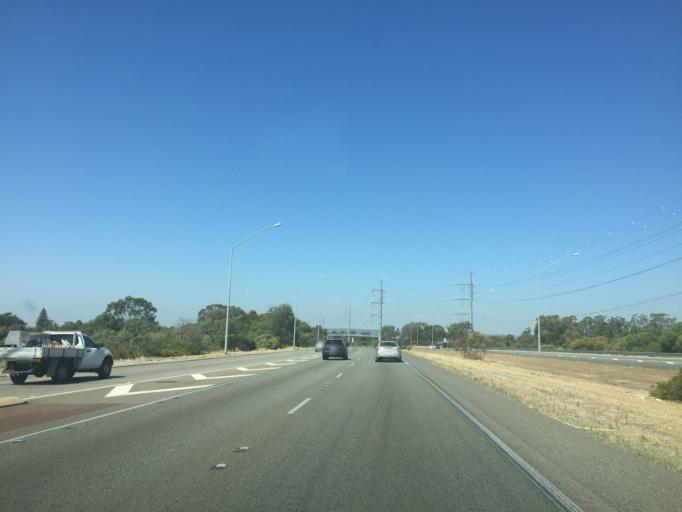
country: AU
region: Western Australia
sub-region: Gosnells
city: Langford
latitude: -32.0526
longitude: 115.9343
